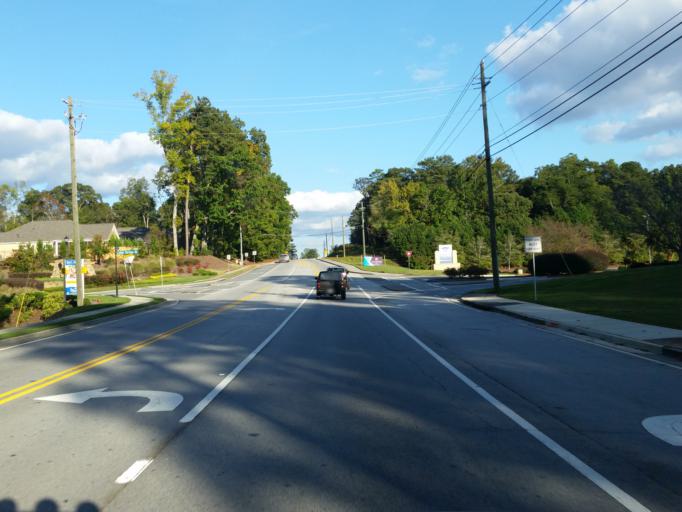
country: US
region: Georgia
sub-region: Cobb County
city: Powder Springs
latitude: 33.9028
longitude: -84.6919
